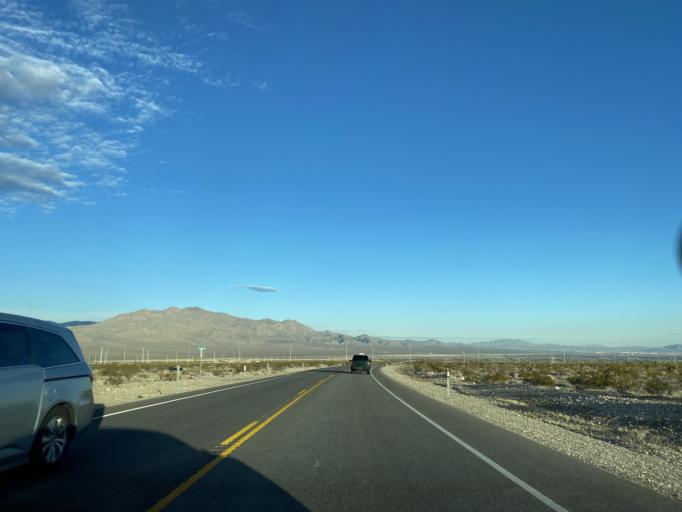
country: US
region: Nevada
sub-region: Clark County
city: Summerlin South
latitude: 36.3248
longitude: -115.3429
